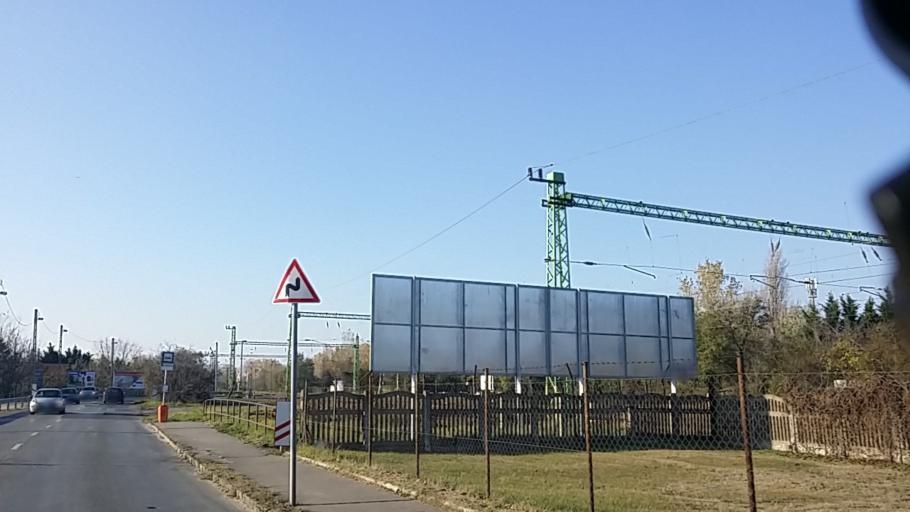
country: HU
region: Budapest
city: Budapest XVII. keruelet
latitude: 47.4697
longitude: 19.2377
